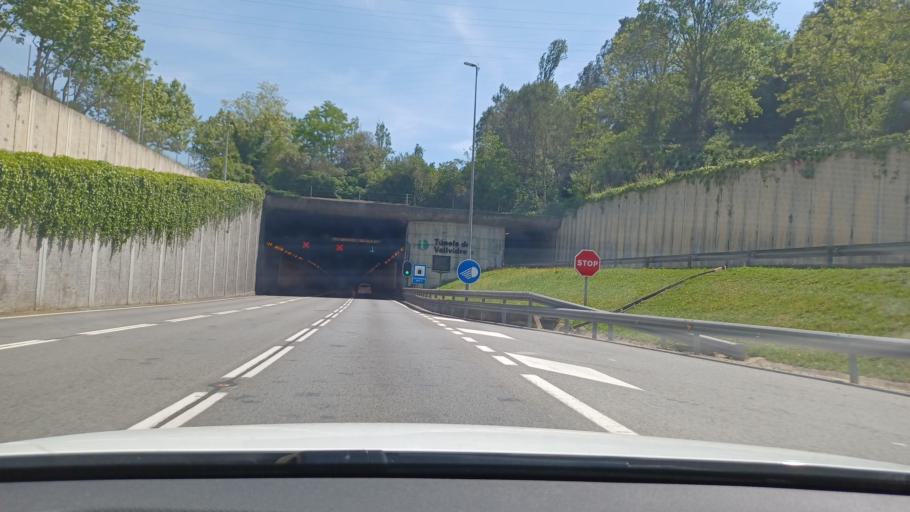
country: ES
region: Catalonia
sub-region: Provincia de Barcelona
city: Sant Just Desvern
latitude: 41.4224
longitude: 2.0941
